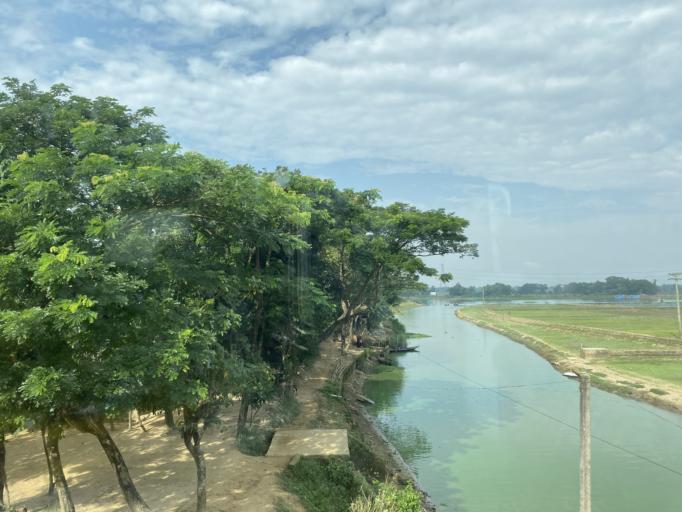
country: IN
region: Tripura
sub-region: West Tripura
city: Agartala
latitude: 23.8837
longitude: 91.2063
